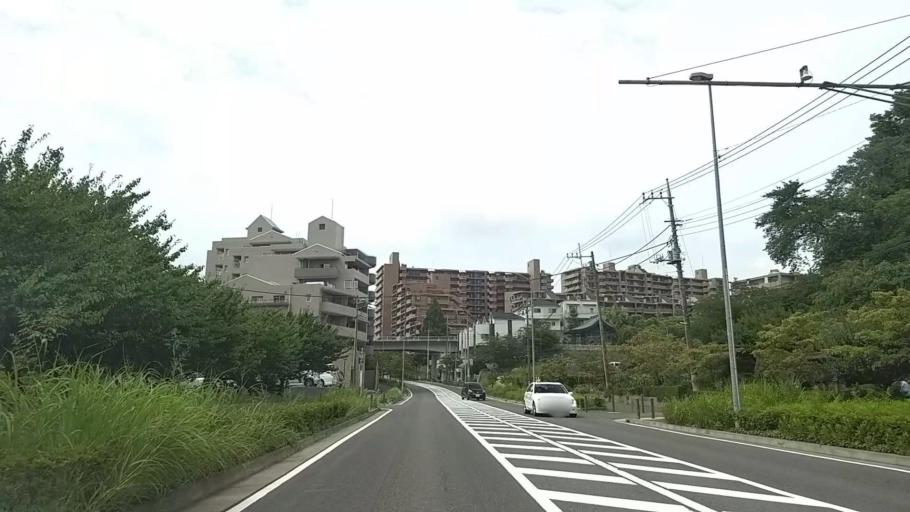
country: JP
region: Kanagawa
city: Yokohama
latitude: 35.5435
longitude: 139.5881
